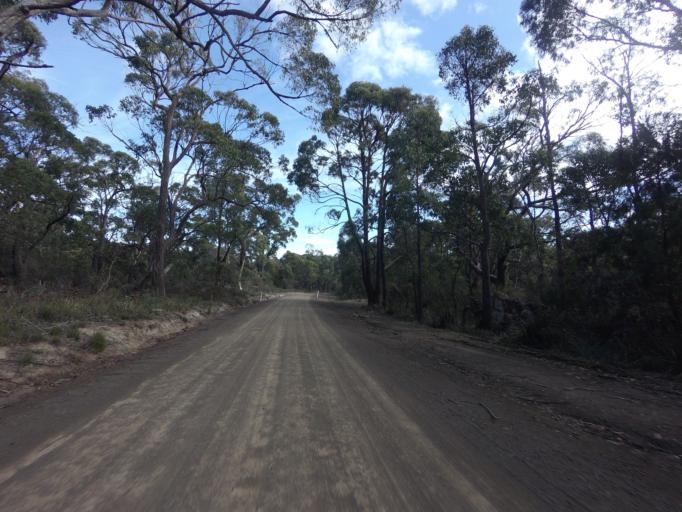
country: AU
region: Tasmania
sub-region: Clarence
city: Sandford
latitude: -43.0891
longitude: 147.7010
